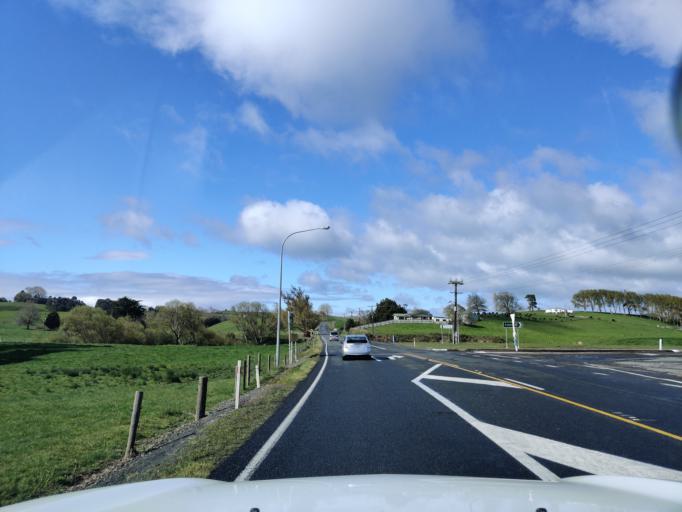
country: NZ
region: Waikato
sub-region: Otorohanga District
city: Otorohanga
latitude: -38.0873
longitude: 175.1818
